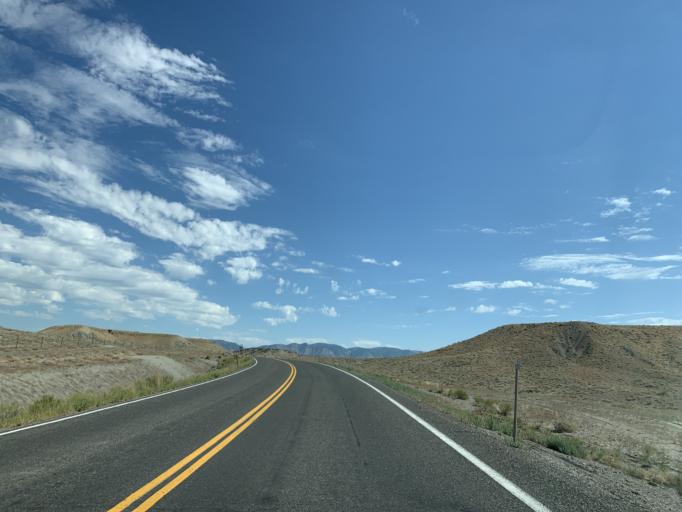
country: US
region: Utah
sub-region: Carbon County
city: Wellington
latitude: 39.5557
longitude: -110.6667
